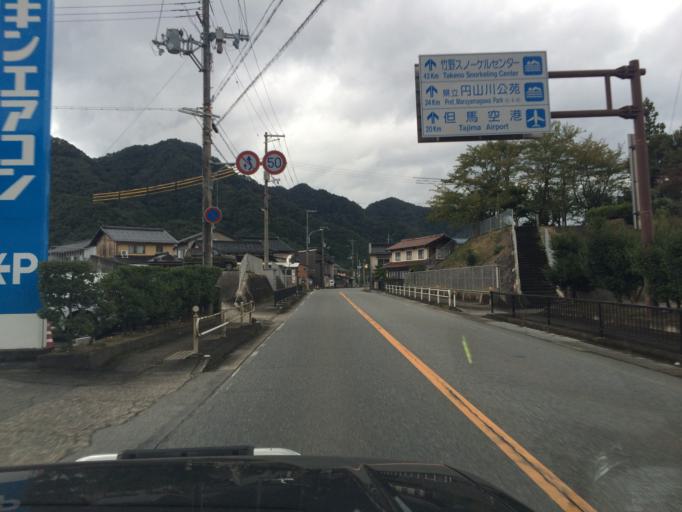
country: JP
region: Hyogo
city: Toyooka
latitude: 35.4038
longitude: 134.7772
